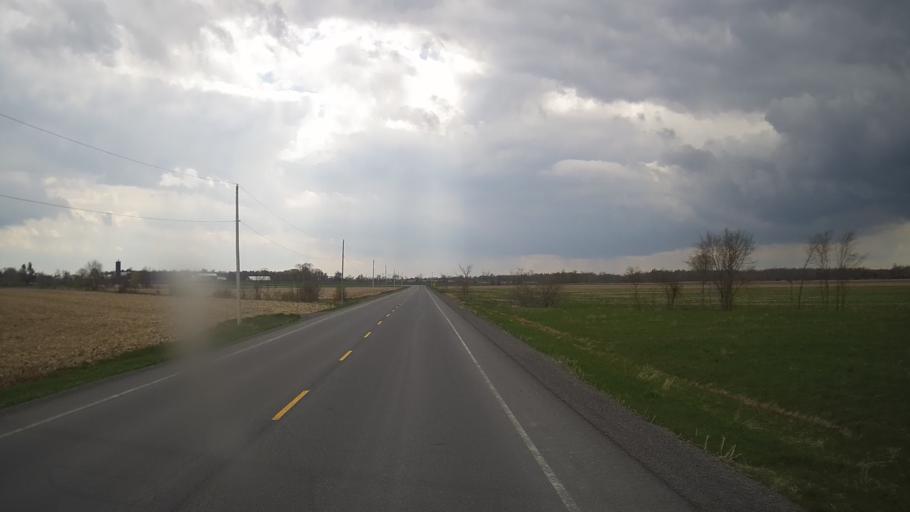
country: CA
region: Ontario
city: Hawkesbury
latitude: 45.5557
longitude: -74.5391
